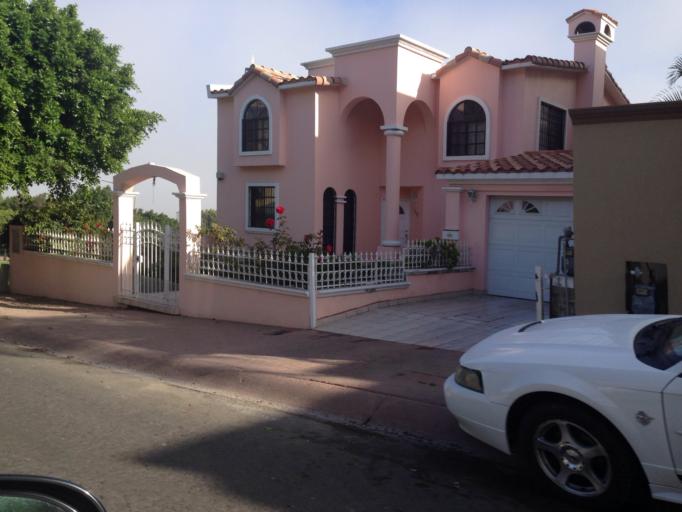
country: MX
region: Baja California
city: Tijuana
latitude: 32.4910
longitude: -117.0024
